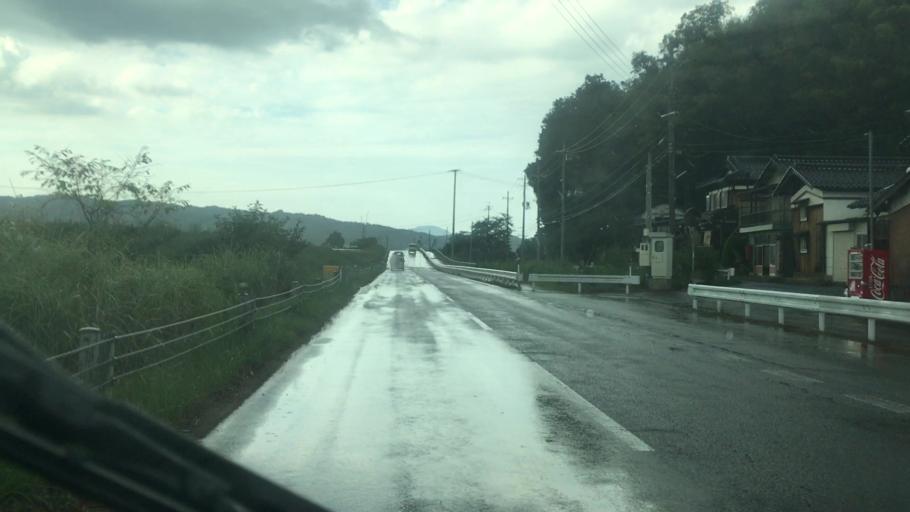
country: JP
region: Hyogo
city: Toyooka
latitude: 35.4868
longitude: 134.8170
